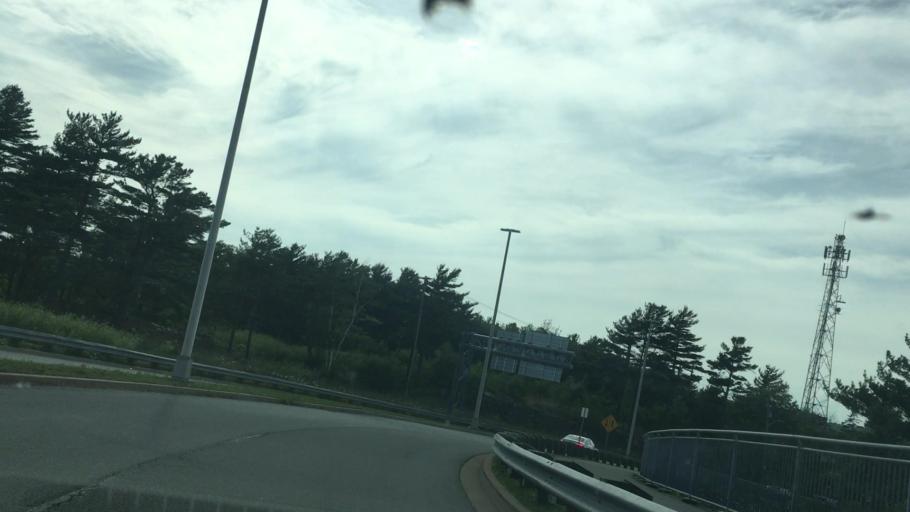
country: CA
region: Nova Scotia
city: Dartmouth
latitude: 44.6982
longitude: -63.6931
